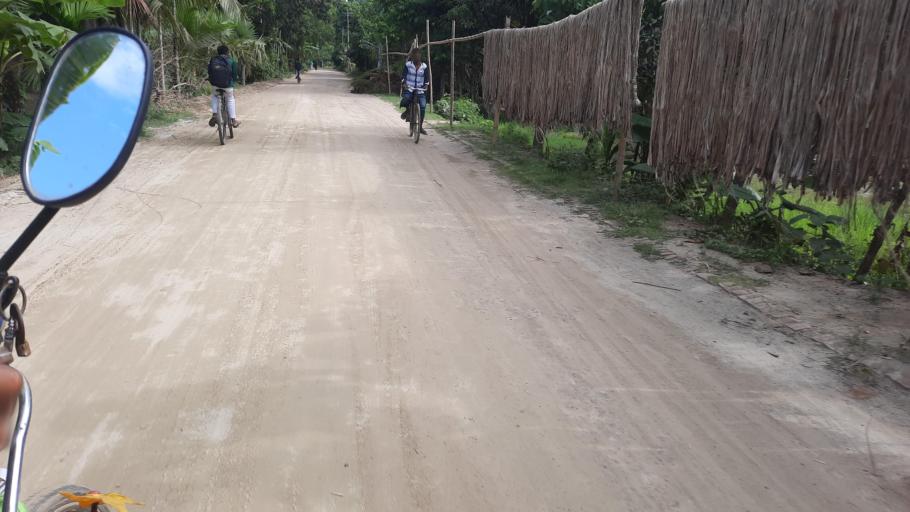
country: BD
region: Khulna
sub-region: Magura
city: Magura
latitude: 23.4676
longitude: 89.6124
